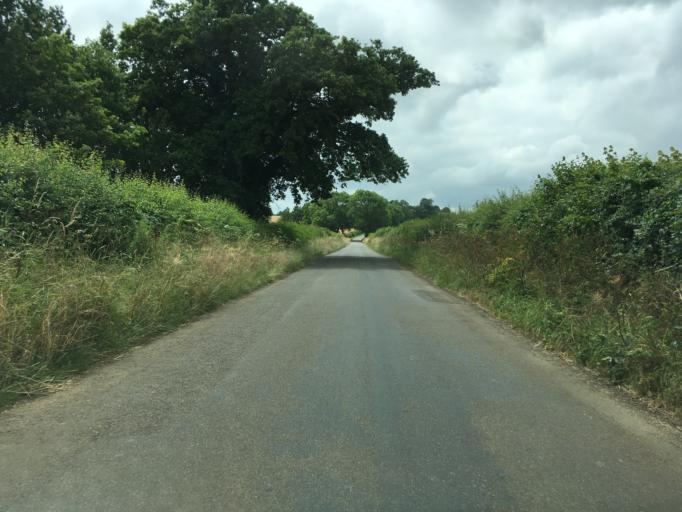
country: GB
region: England
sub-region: Oxfordshire
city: Bloxham
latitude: 51.9654
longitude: -1.3889
